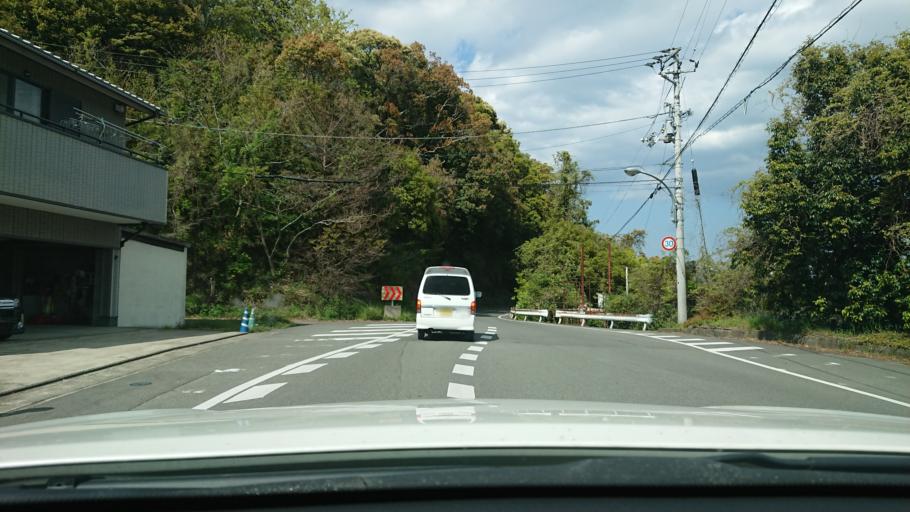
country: JP
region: Tokushima
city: Komatsushimacho
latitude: 34.0036
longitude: 134.5499
